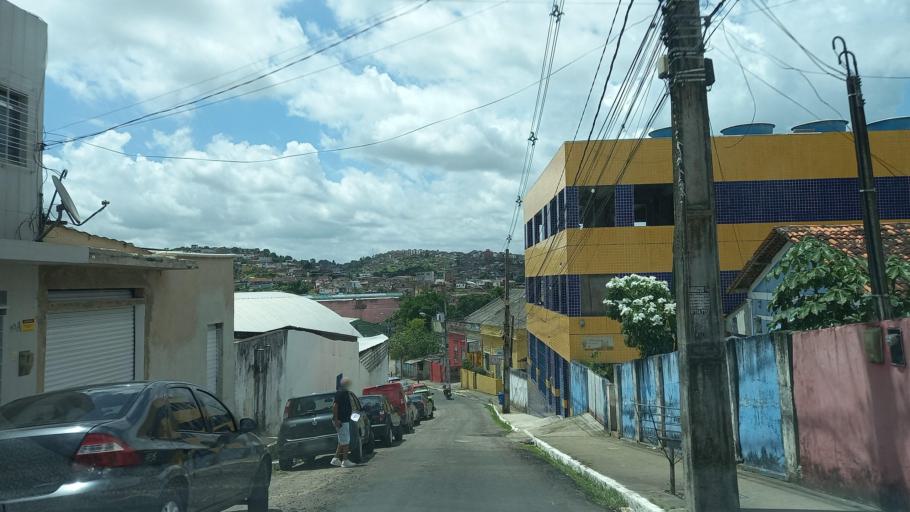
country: BR
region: Pernambuco
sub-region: Jaboatao Dos Guararapes
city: Jaboatao dos Guararapes
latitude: -8.1117
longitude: -35.0197
